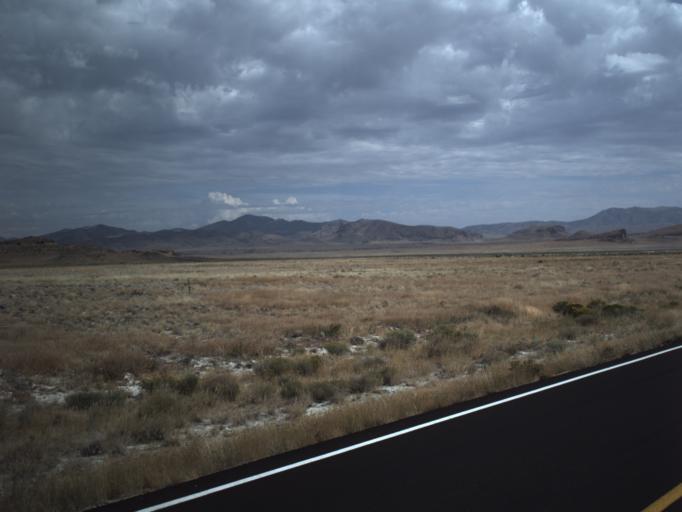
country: US
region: Utah
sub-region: Tooele County
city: Wendover
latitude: 41.4217
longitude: -113.8876
